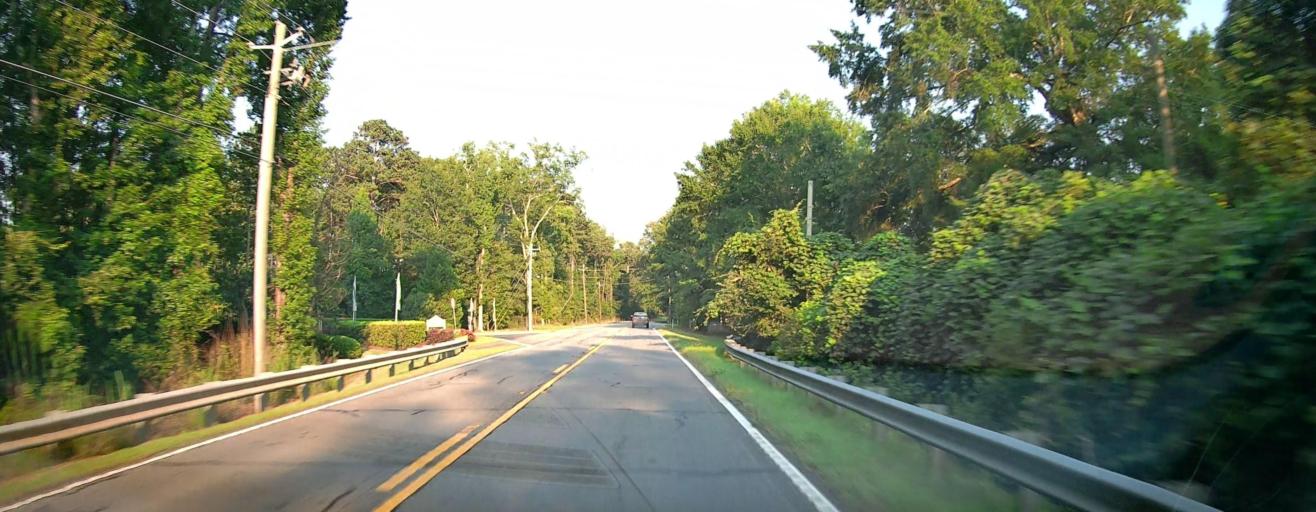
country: US
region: Georgia
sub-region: Bibb County
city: Macon
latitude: 32.8849
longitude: -83.7336
